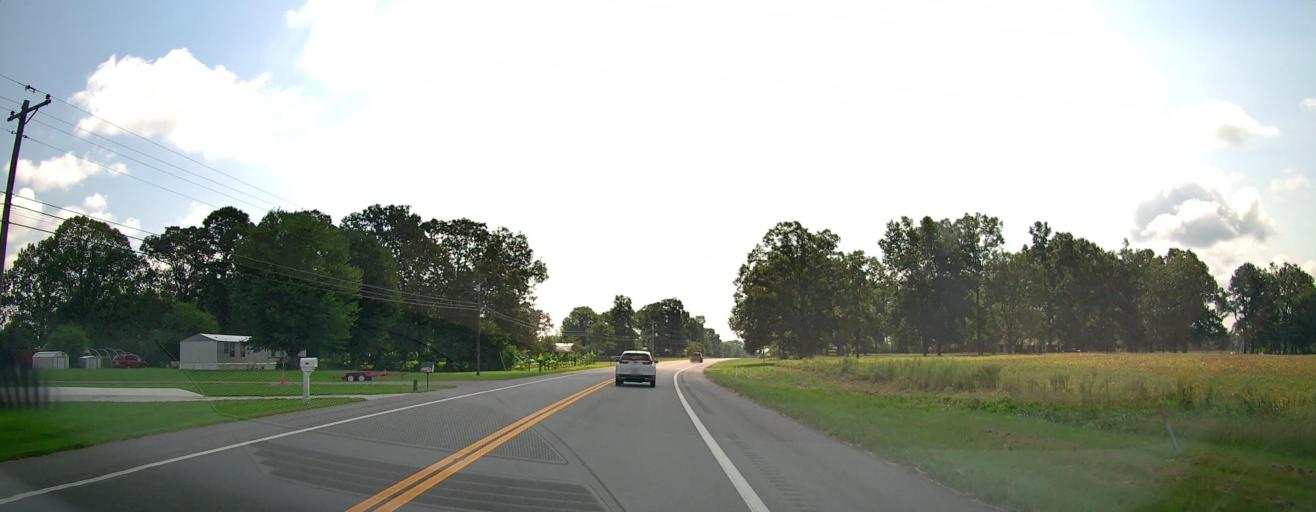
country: US
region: Tennessee
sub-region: Coffee County
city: New Union
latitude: 35.5146
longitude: -86.1284
